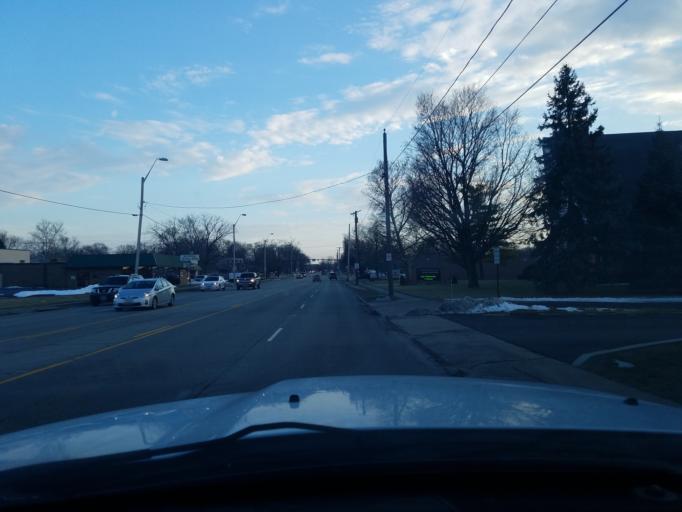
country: US
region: Ohio
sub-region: Montgomery County
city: Kettering
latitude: 39.7015
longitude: -84.1418
